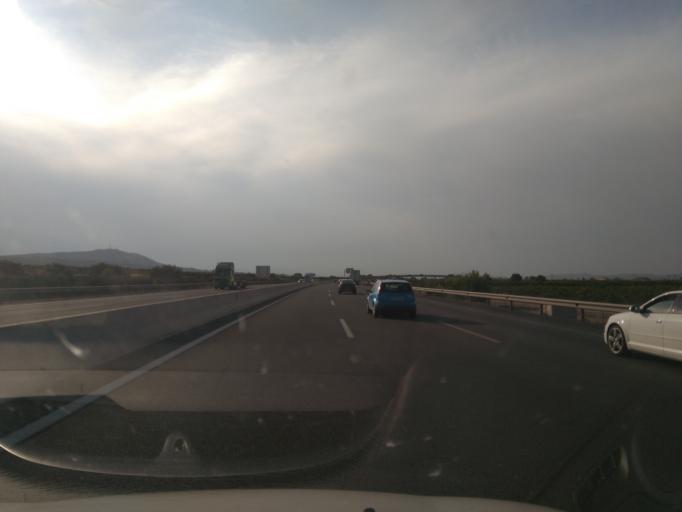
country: ES
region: Valencia
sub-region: Provincia de Valencia
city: Torrent
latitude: 39.4235
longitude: -0.5199
